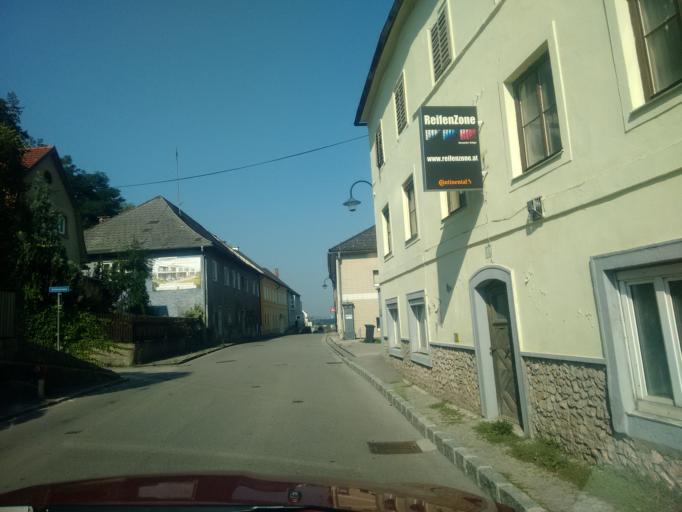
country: AT
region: Upper Austria
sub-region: Wels-Land
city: Thalheim bei Wels
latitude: 48.1516
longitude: 14.0308
